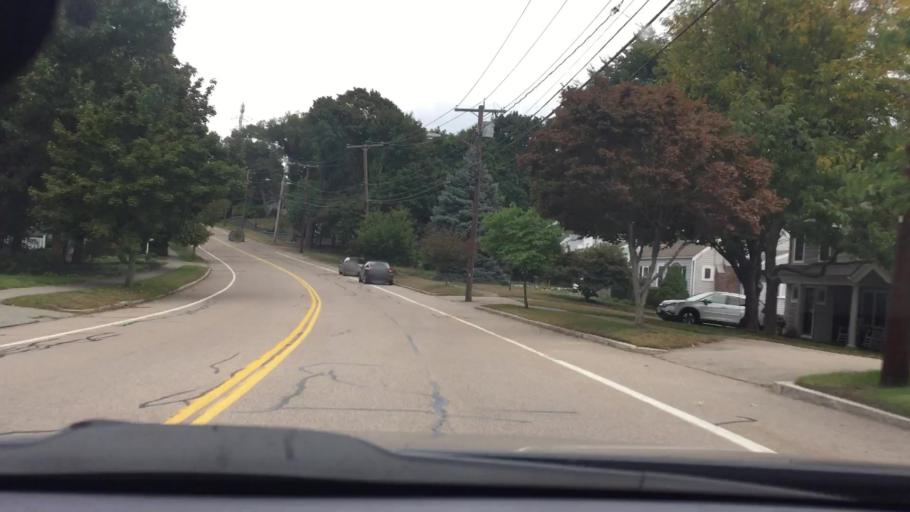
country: US
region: Massachusetts
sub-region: Norfolk County
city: Needham
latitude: 42.2747
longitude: -71.2043
